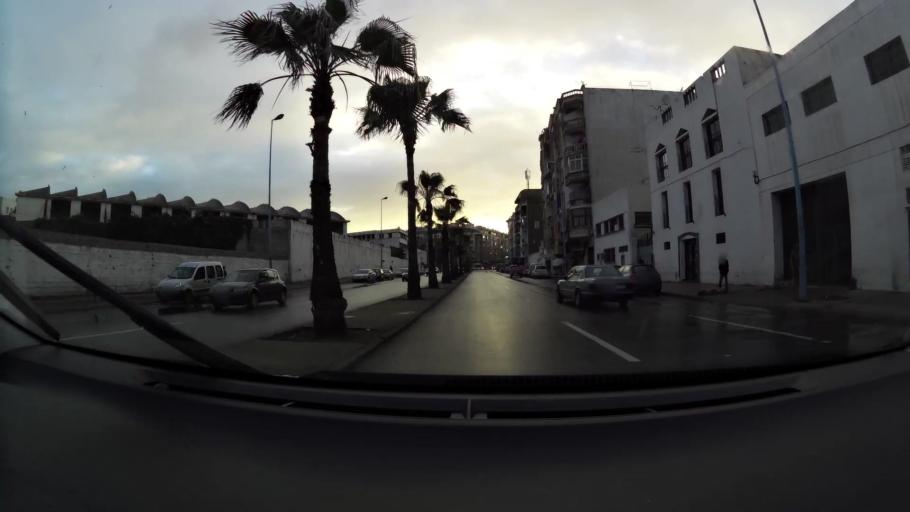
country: MA
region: Grand Casablanca
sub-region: Casablanca
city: Casablanca
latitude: 33.5853
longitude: -7.5777
